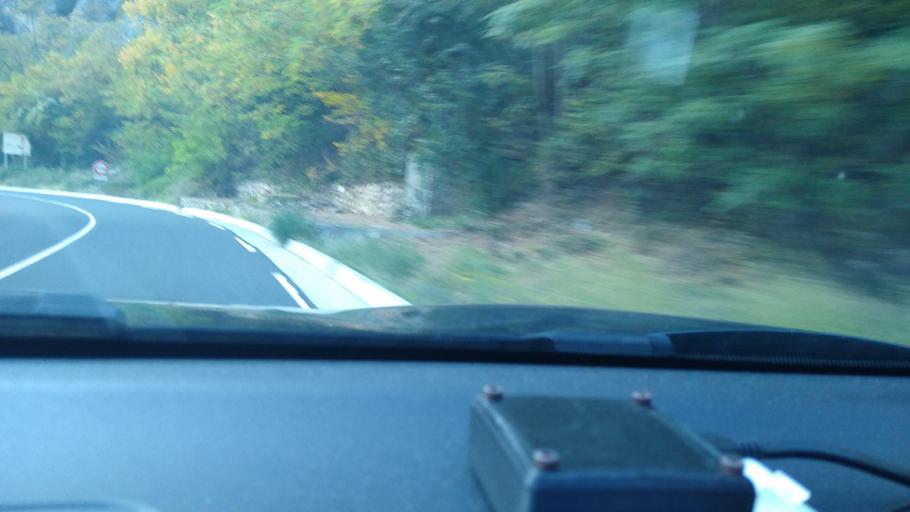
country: FR
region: Languedoc-Roussillon
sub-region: Departement des Pyrenees-Orientales
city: Vernet-les-Bains
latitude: 42.5258
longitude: 2.2246
